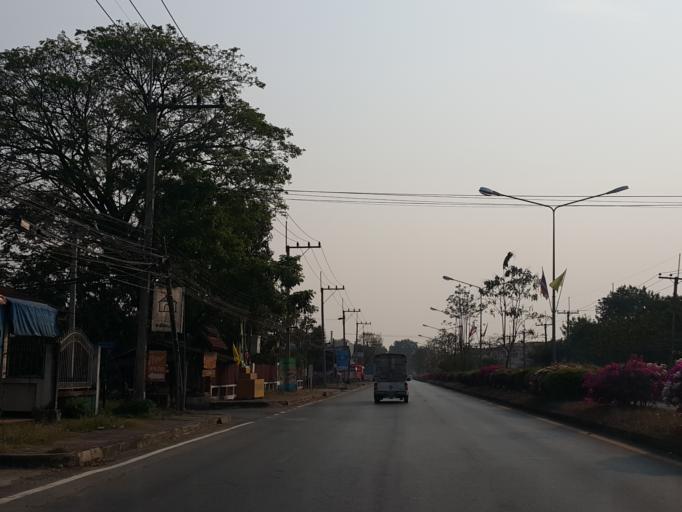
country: TH
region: Lampang
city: Lampang
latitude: 18.3117
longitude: 99.5162
